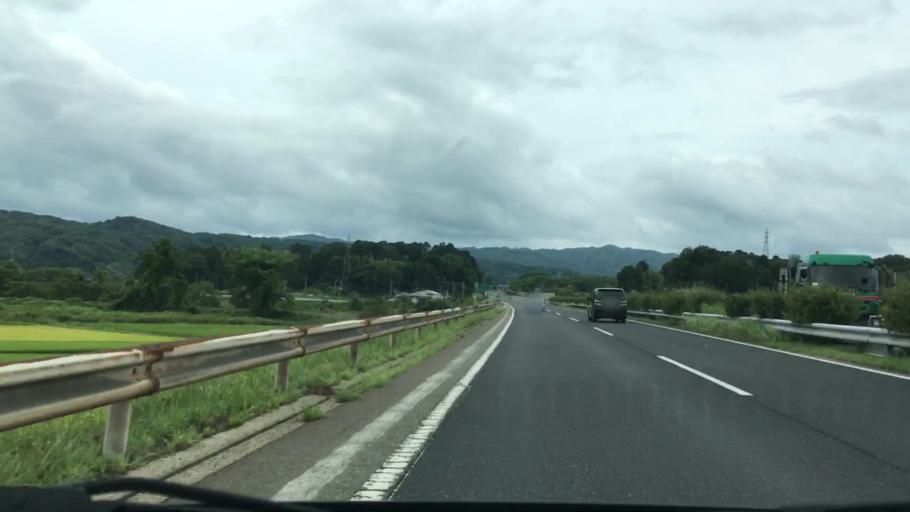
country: JP
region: Okayama
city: Tsuyama
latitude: 35.0623
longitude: 133.9366
